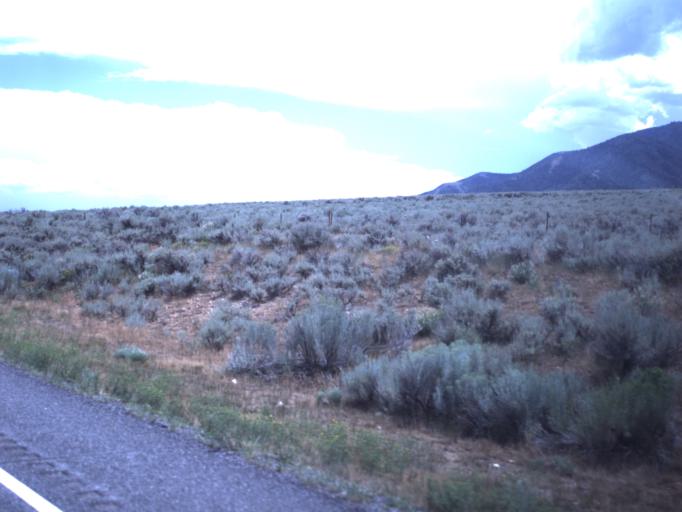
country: US
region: Utah
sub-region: Sanpete County
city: Fountain Green
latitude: 39.6914
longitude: -111.6865
